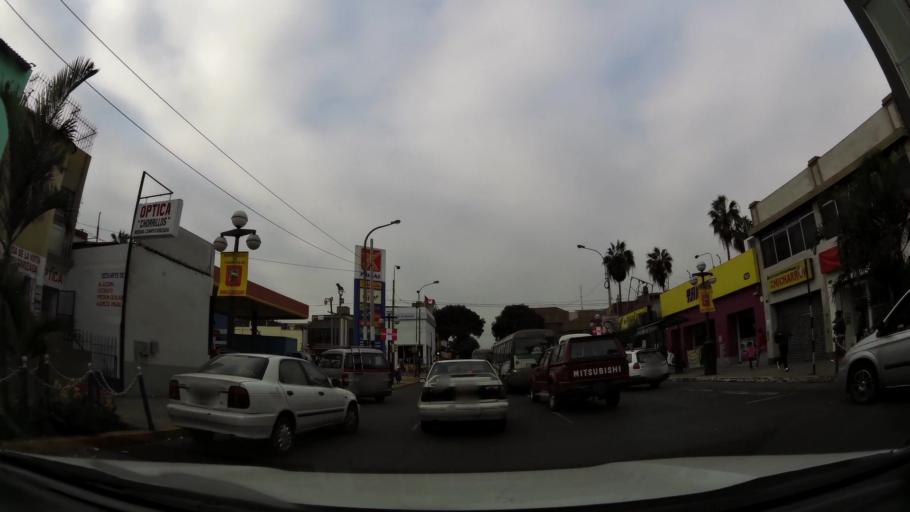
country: PE
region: Lima
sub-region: Lima
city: Surco
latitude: -12.1682
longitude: -77.0257
